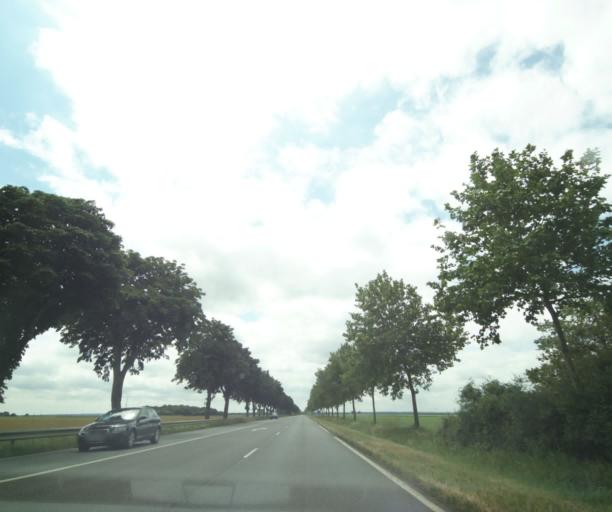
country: FR
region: Poitou-Charentes
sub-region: Departement des Deux-Sevres
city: Saint-Jean-de-Thouars
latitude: 46.9467
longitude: -0.2048
